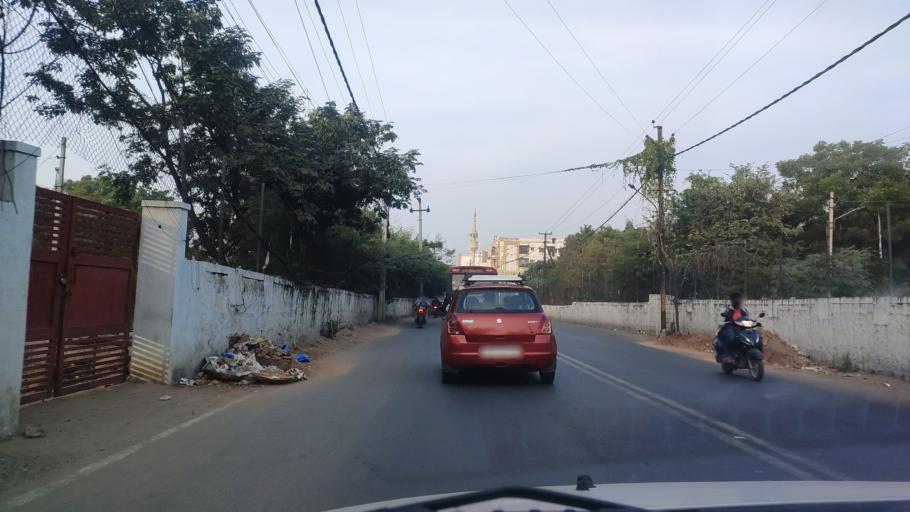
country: IN
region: Telangana
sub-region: Rangareddi
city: Gaddi Annaram
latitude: 17.3918
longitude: 78.5145
